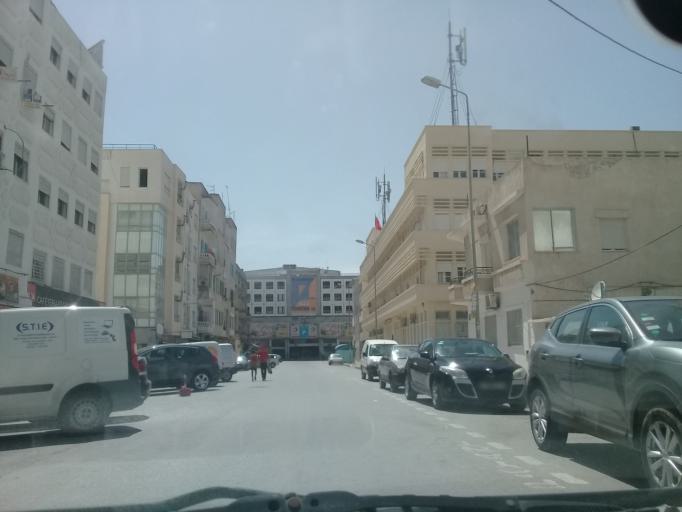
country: TN
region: Tunis
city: Tunis
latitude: 36.8127
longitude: 10.1831
